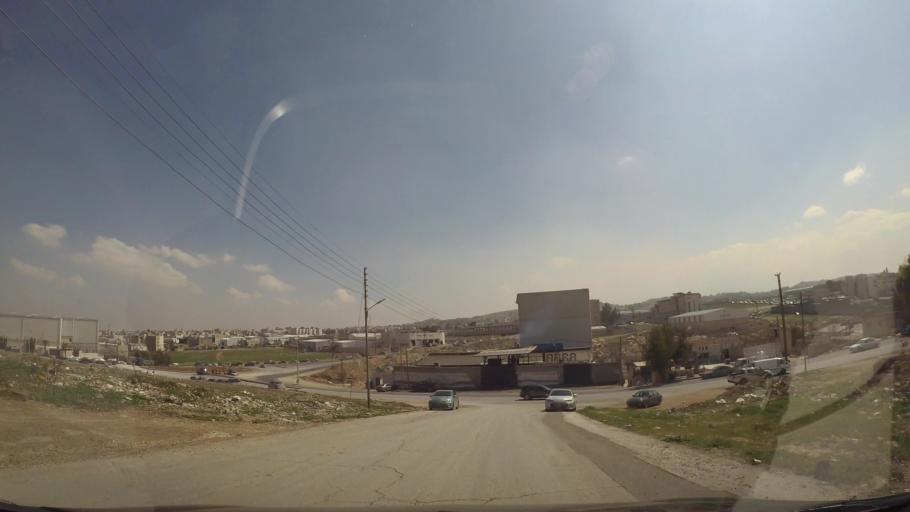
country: JO
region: Zarqa
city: Russeifa
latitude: 31.9876
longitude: 36.0070
